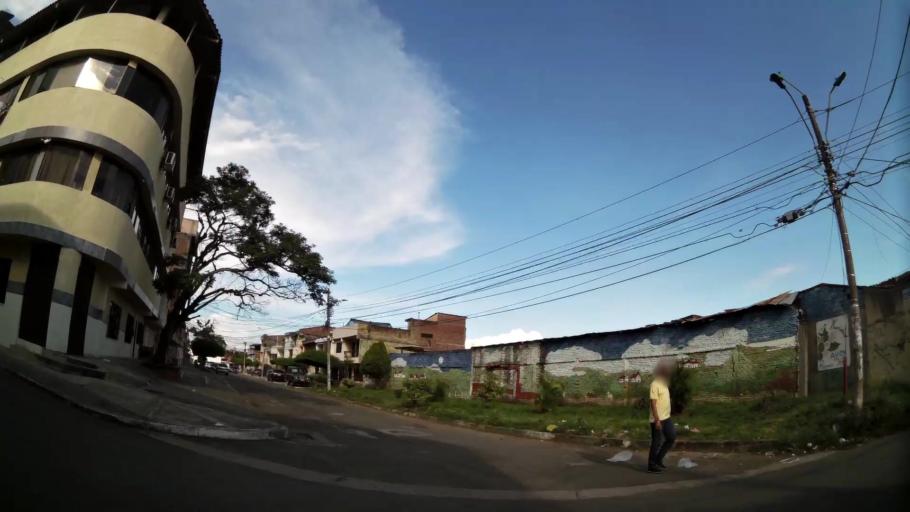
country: CO
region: Valle del Cauca
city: Cali
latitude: 3.4288
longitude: -76.5270
